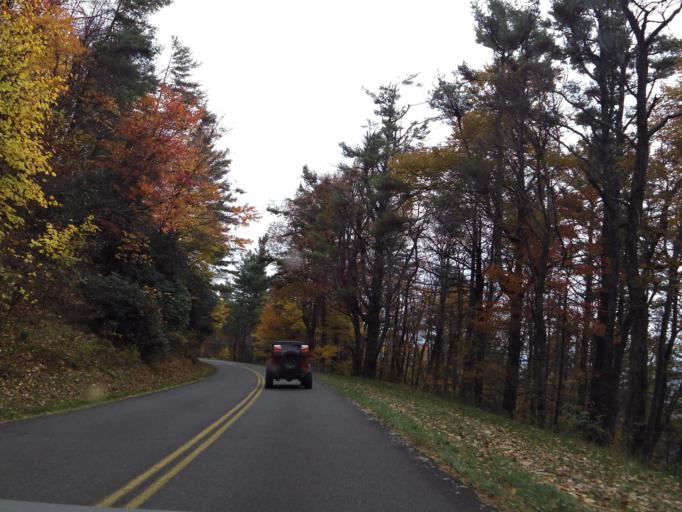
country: US
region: North Carolina
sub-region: Ashe County
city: West Jefferson
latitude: 36.2390
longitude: -81.4953
